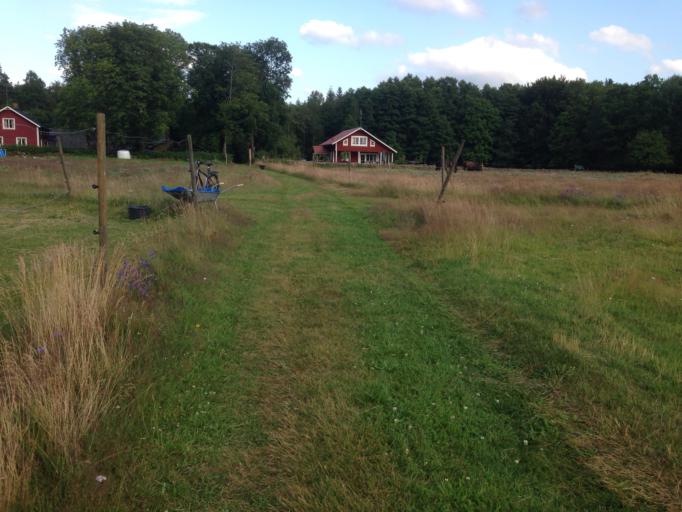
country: SE
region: Kronoberg
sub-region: Ljungby Kommun
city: Ljungby
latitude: 56.8679
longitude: 13.7822
